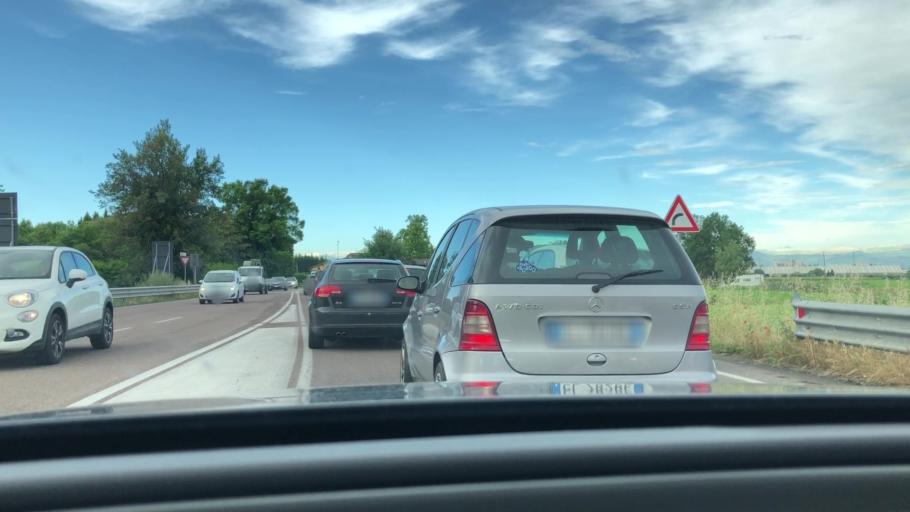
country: IT
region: Emilia-Romagna
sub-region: Provincia di Modena
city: San Damaso
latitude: 44.6101
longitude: 10.9358
